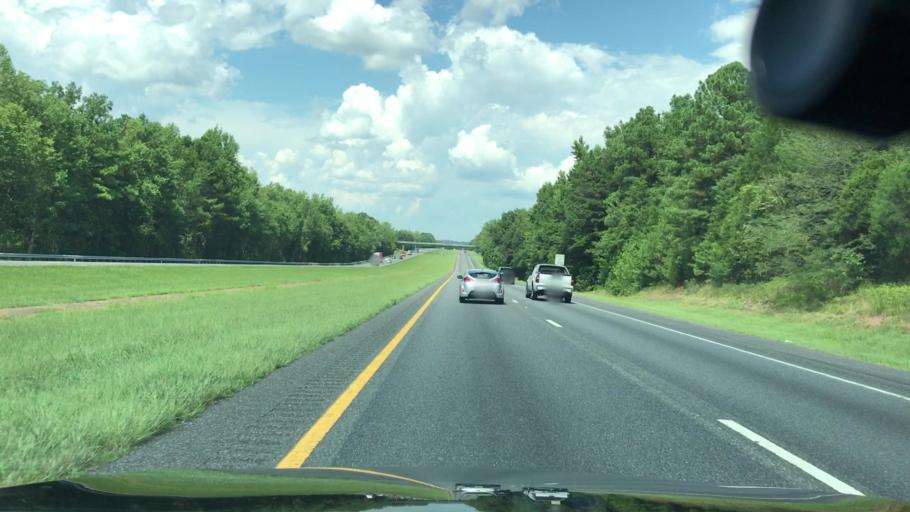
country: US
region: South Carolina
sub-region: York County
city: Lesslie
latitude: 34.8654
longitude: -81.0041
